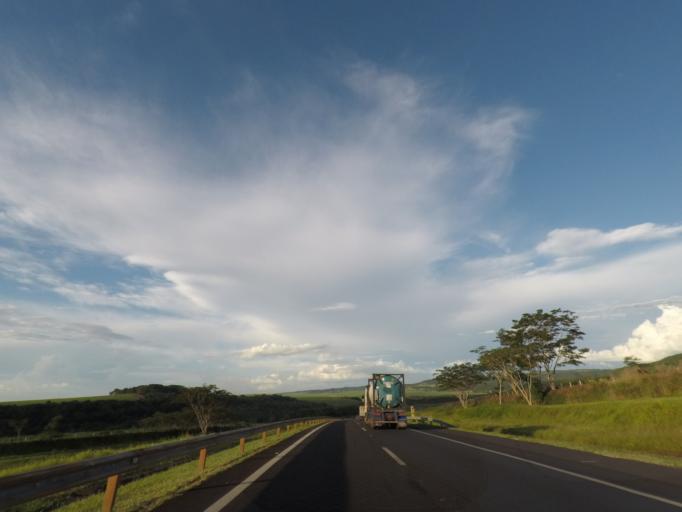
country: BR
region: Sao Paulo
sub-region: Ituverava
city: Ituverava
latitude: -20.2454
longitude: -47.7979
